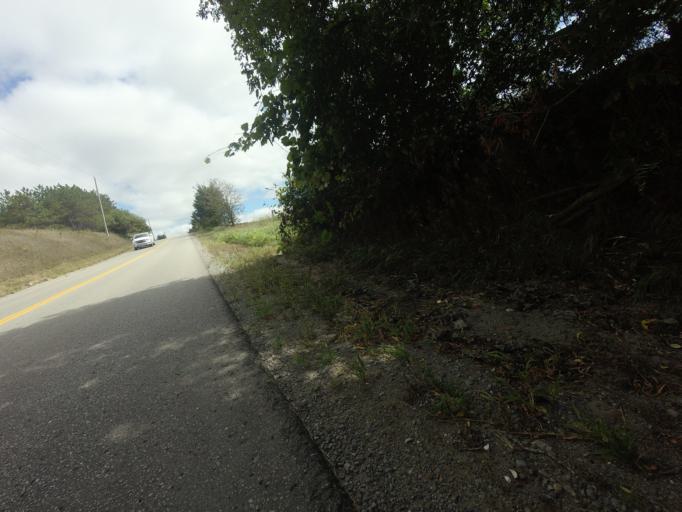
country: CA
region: Ontario
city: Uxbridge
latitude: 44.1126
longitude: -79.2251
